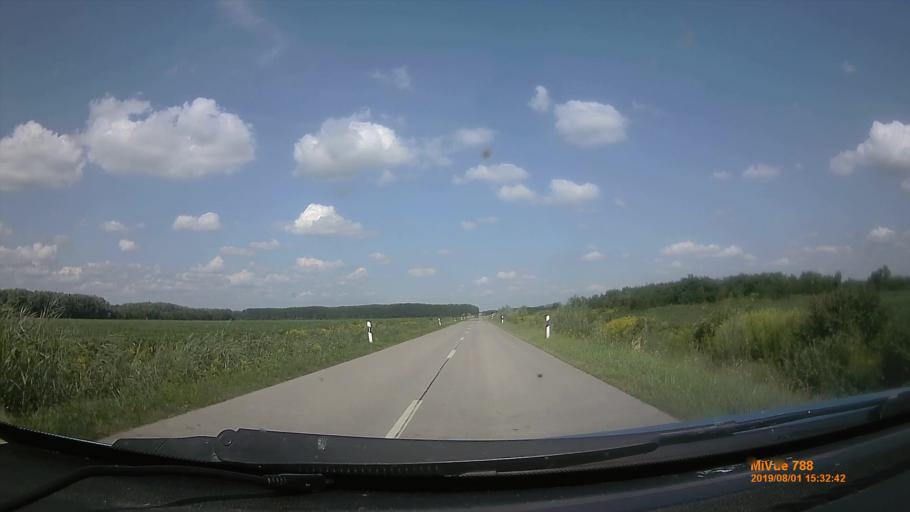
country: HU
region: Baranya
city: Sellye
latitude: 45.9509
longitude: 17.8678
